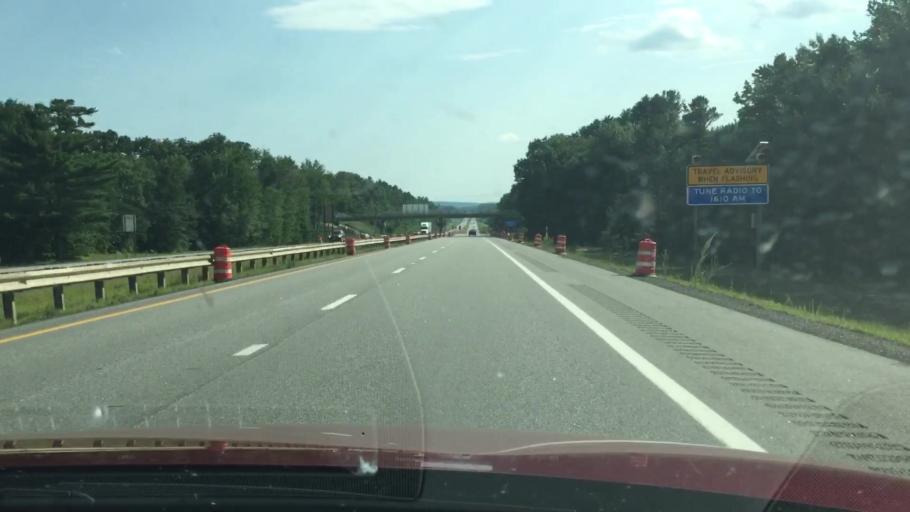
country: US
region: Maine
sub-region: Cumberland County
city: New Gloucester
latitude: 43.9262
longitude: -70.3369
